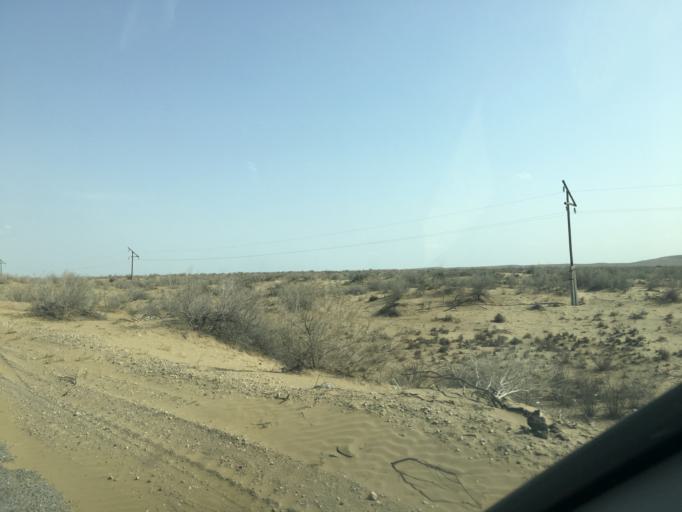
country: TM
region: Lebap
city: Farap
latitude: 39.3281
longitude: 63.3360
